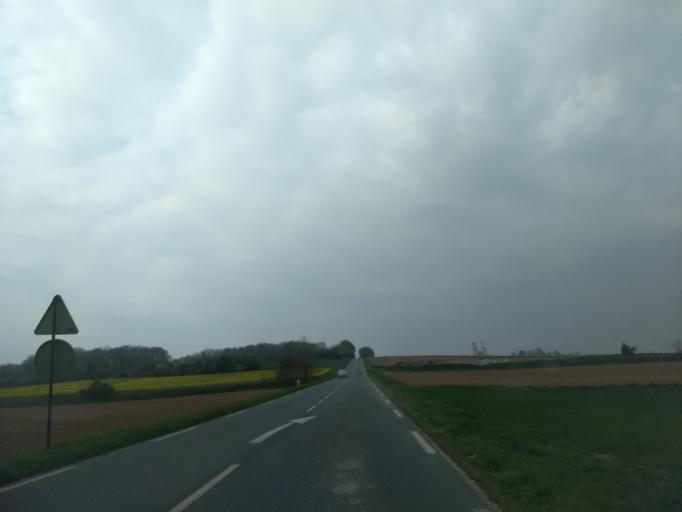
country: FR
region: Nord-Pas-de-Calais
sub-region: Departement du Pas-de-Calais
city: Maroeuil
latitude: 50.3400
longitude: 2.7028
